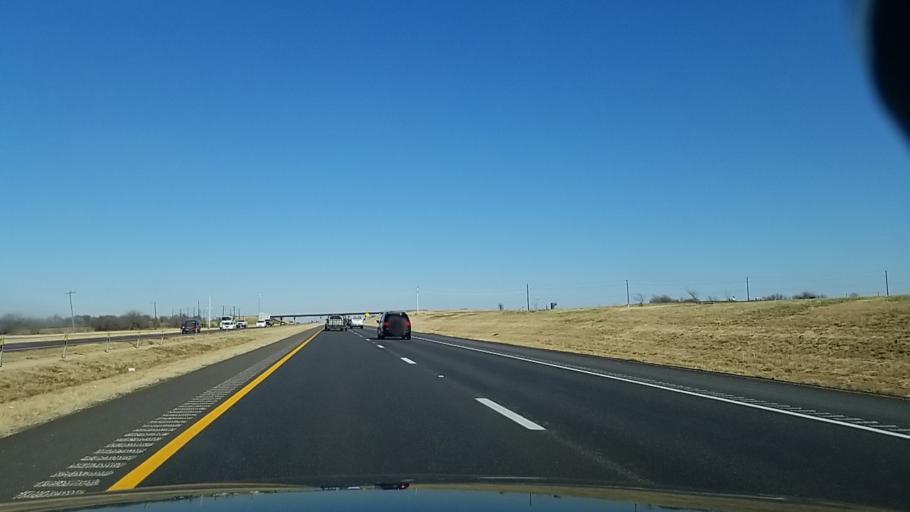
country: US
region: Texas
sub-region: Denton County
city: Justin
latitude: 33.0752
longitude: -97.2379
